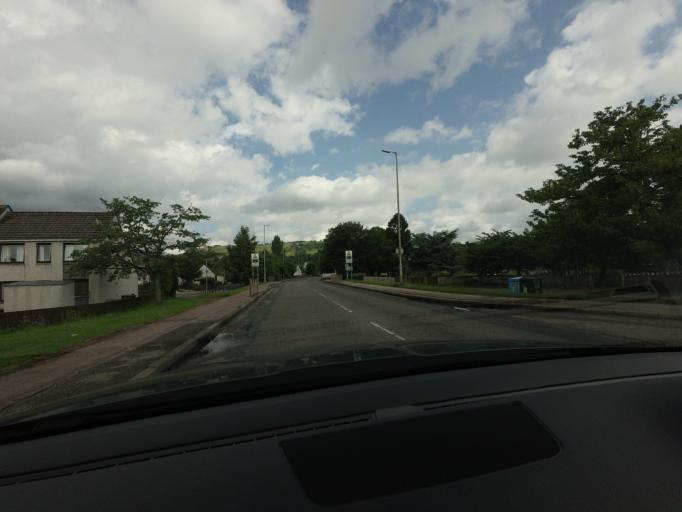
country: GB
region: Scotland
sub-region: Highland
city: Dingwall
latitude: 57.5981
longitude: -4.4321
